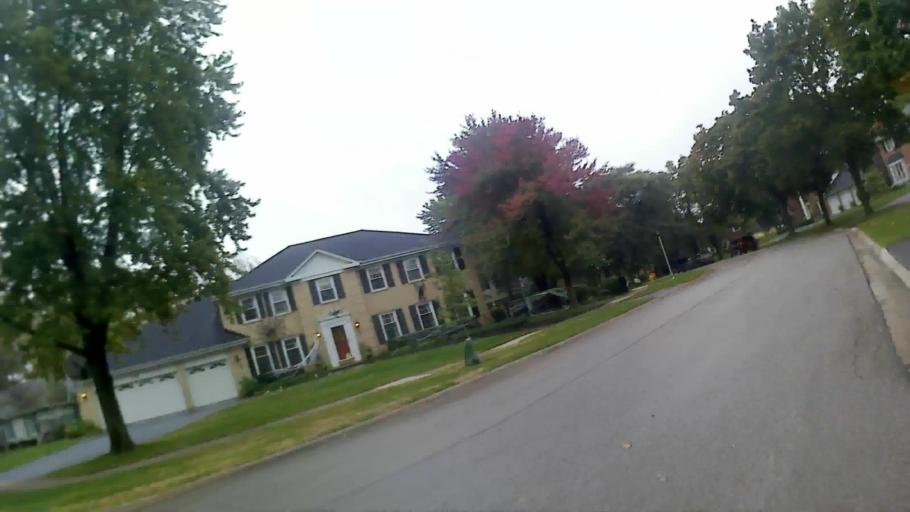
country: US
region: Illinois
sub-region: DuPage County
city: Wheaton
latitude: 41.8418
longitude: -88.1079
